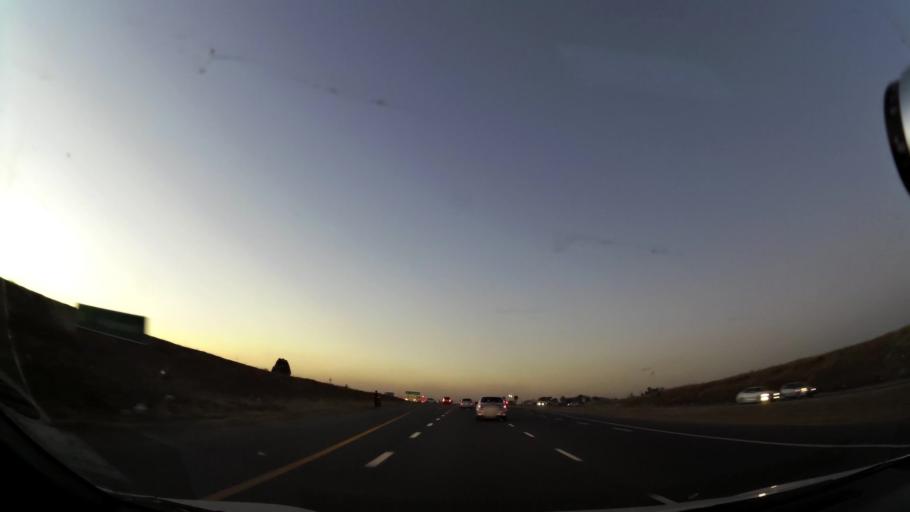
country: ZA
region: Gauteng
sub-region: City of Johannesburg Metropolitan Municipality
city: Diepsloot
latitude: -25.9106
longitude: 28.0264
